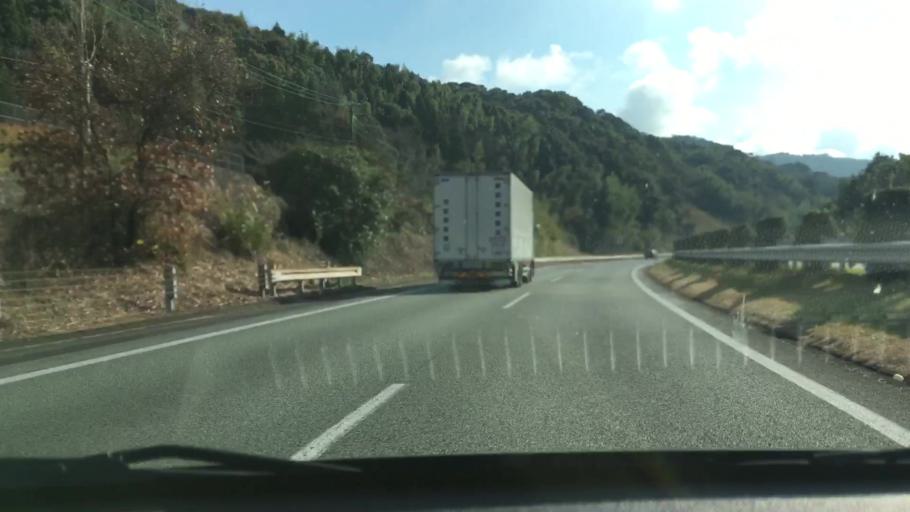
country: JP
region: Kumamoto
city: Matsubase
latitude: 32.6121
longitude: 130.7247
